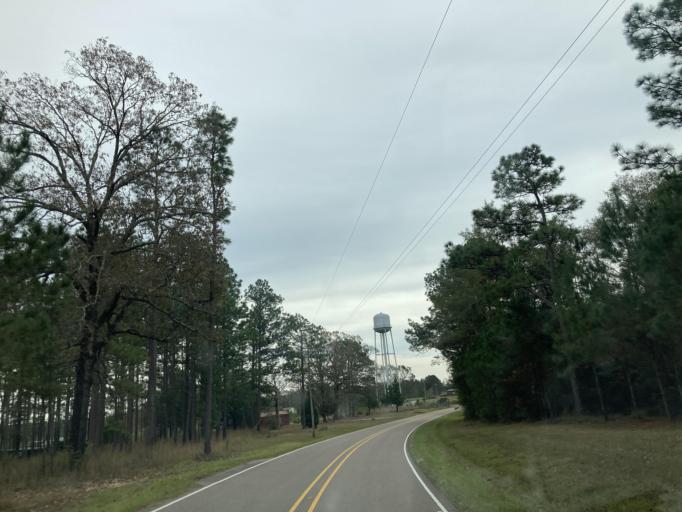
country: US
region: Mississippi
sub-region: Lamar County
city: Lumberton
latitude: 31.0555
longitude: -89.4759
